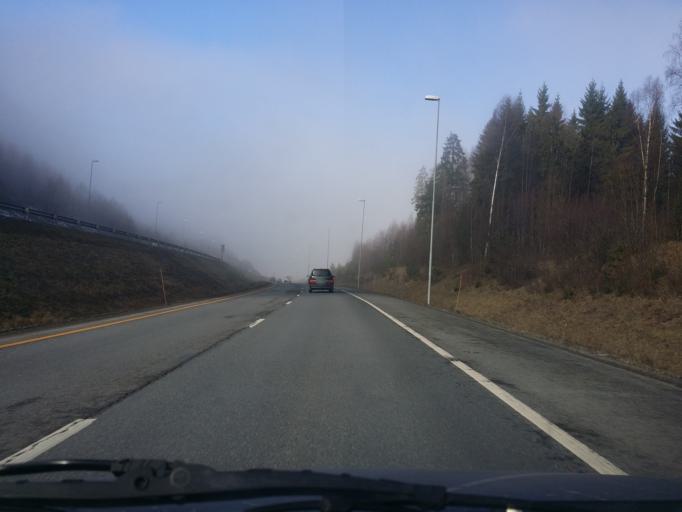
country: NO
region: Buskerud
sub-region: Nedre Eiker
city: Mjondalen
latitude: 59.7459
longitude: 10.0648
